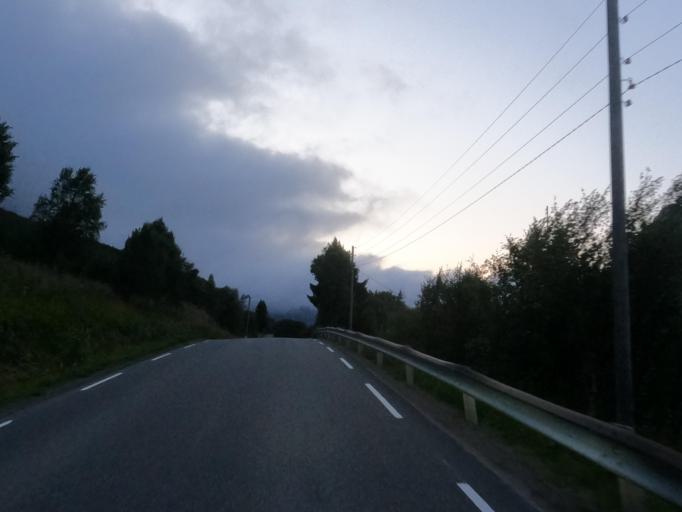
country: NO
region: Nordland
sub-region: Lodingen
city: Lodingen
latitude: 68.5834
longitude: 15.7921
